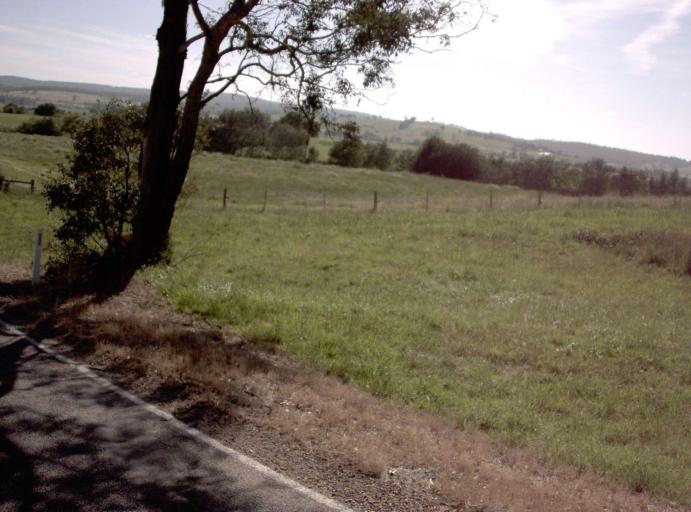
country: AU
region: Victoria
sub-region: East Gippsland
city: Lakes Entrance
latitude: -37.7412
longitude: 147.8180
